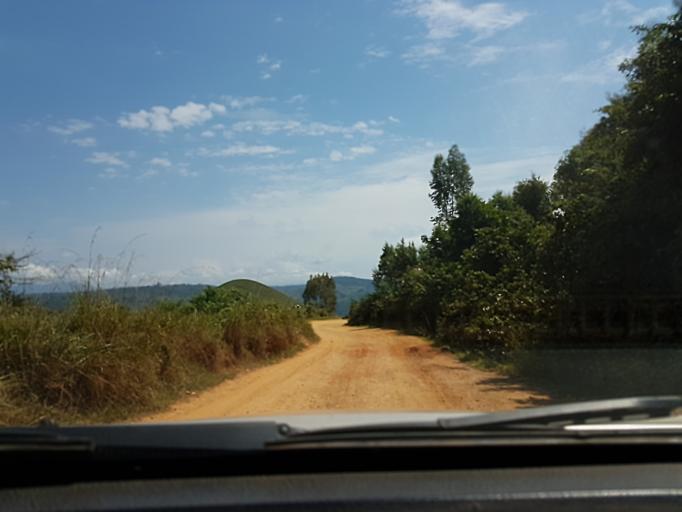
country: RW
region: Western Province
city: Cyangugu
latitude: -2.7024
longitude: 28.9141
